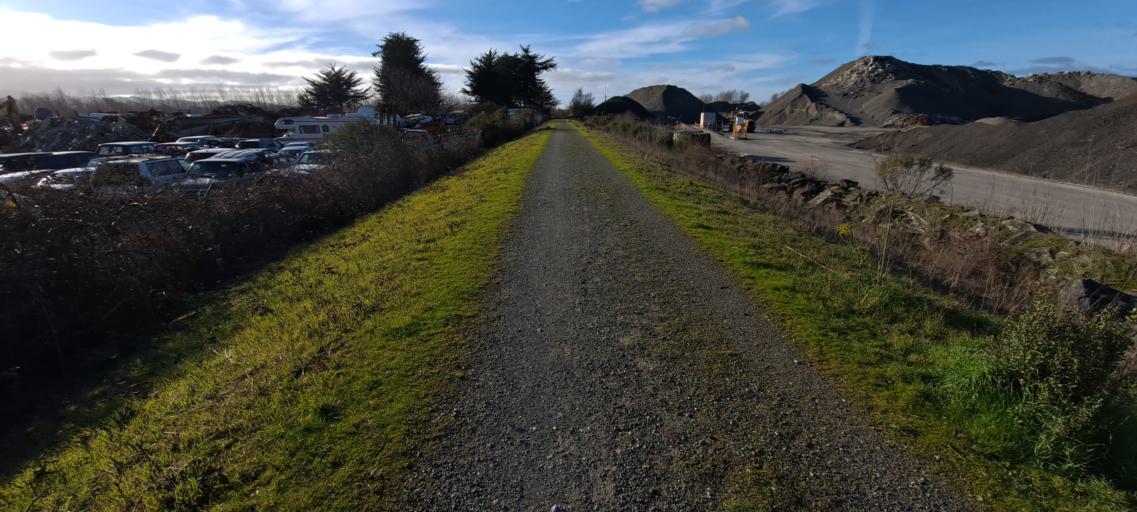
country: US
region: California
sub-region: Humboldt County
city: Fortuna
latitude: 40.5861
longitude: -124.1572
